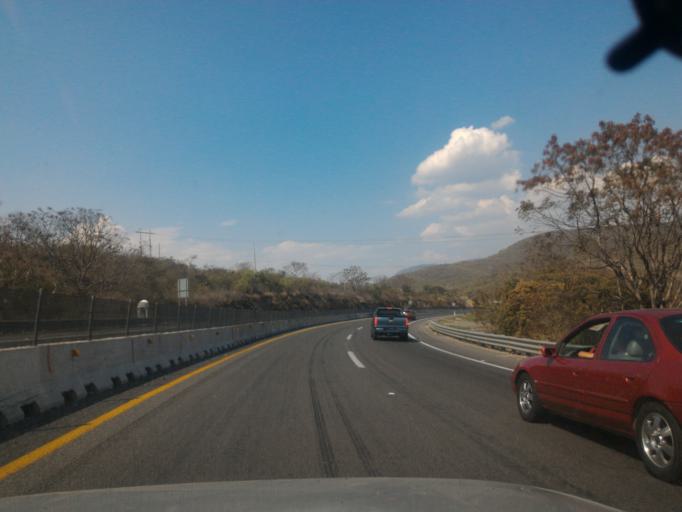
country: MX
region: Jalisco
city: Usmajac
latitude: 19.8514
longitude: -103.5078
